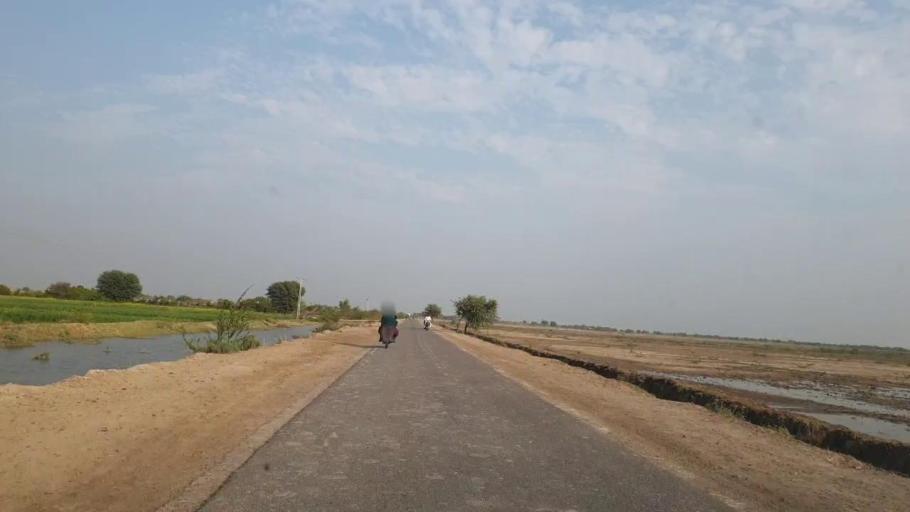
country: PK
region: Sindh
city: Pithoro
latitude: 25.5854
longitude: 69.3409
